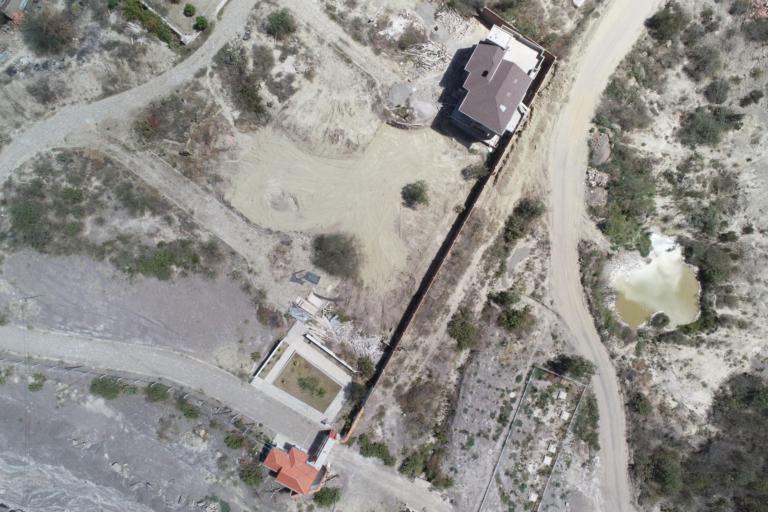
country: BO
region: La Paz
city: La Paz
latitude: -16.6506
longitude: -68.0395
